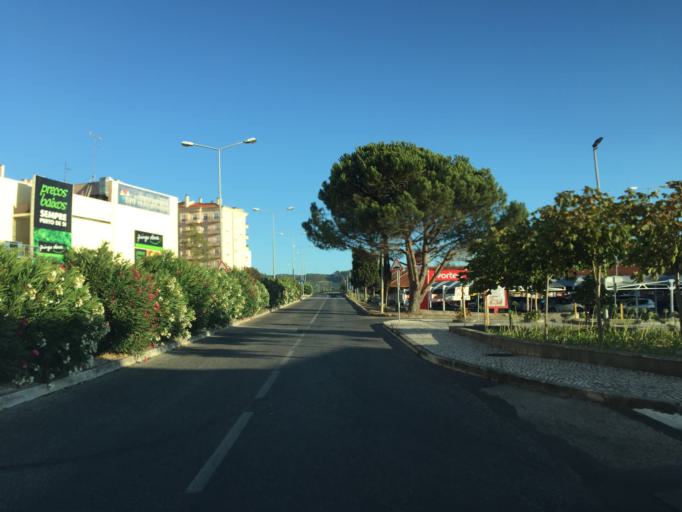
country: PT
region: Lisbon
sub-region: Torres Vedras
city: Torres Vedras
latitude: 39.0820
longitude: -9.2602
